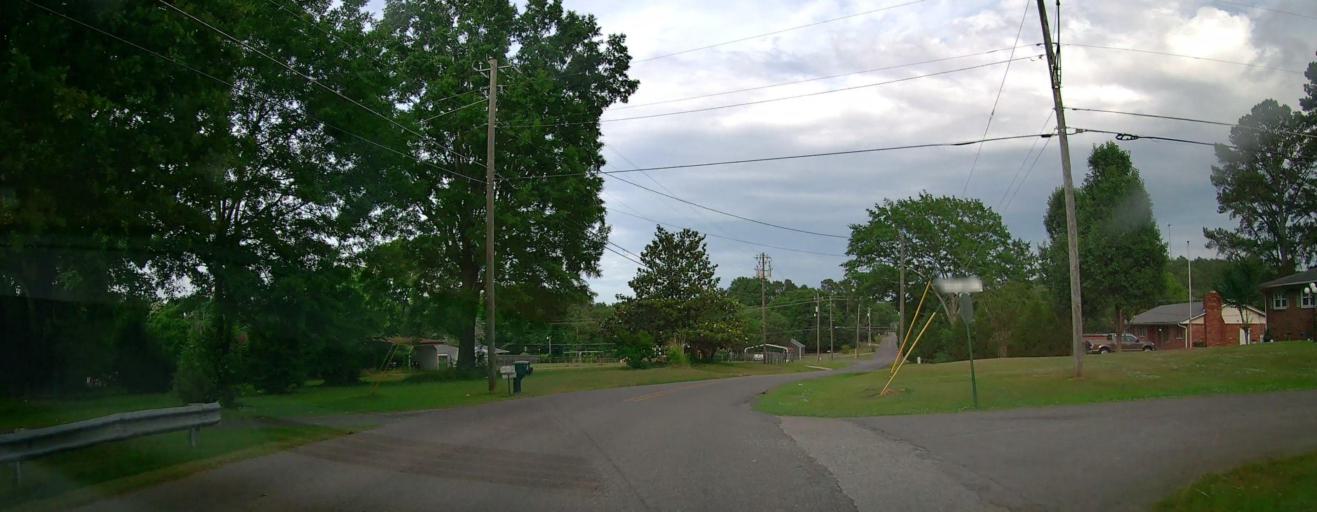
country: US
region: Alabama
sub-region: Calhoun County
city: Oxford
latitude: 33.5855
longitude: -85.8228
